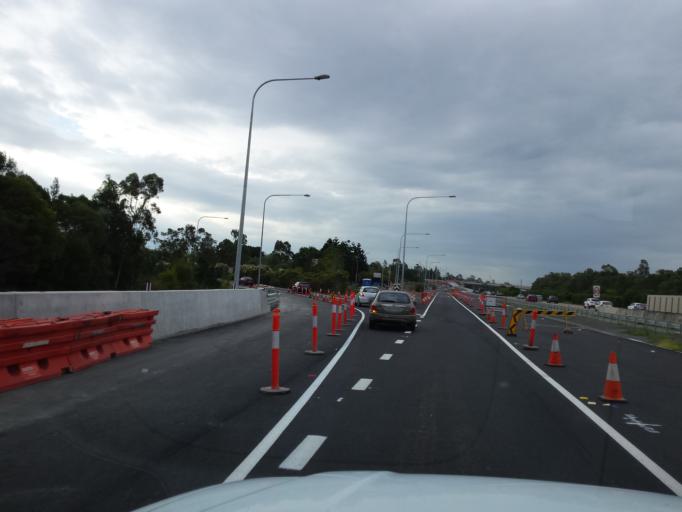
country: AU
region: Queensland
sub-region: Gold Coast
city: Oxenford
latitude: -27.8633
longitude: 153.3110
